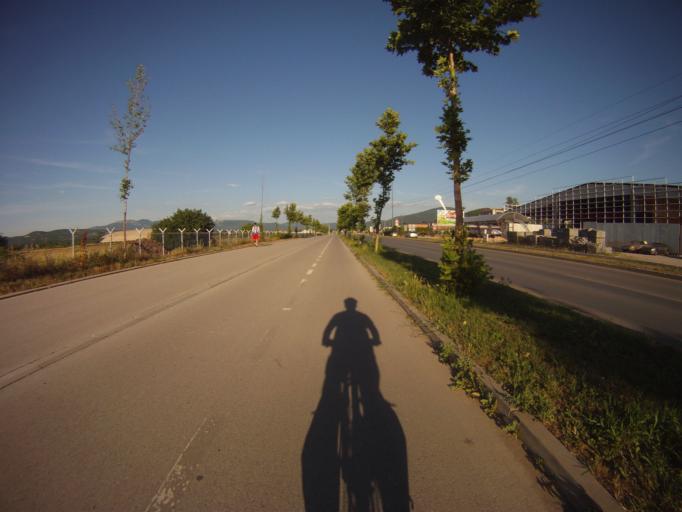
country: RS
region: Central Serbia
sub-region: Nisavski Okrug
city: Nis
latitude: 43.3089
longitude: 21.9447
